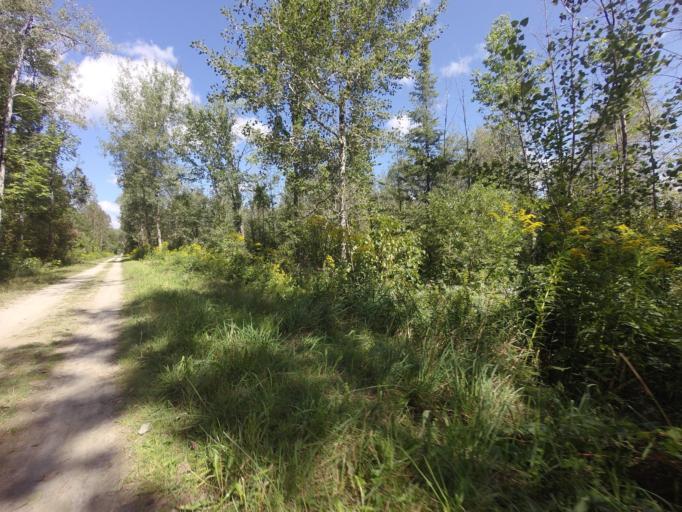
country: CA
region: Ontario
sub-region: Wellington County
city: Guelph
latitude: 43.7497
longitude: -80.3188
